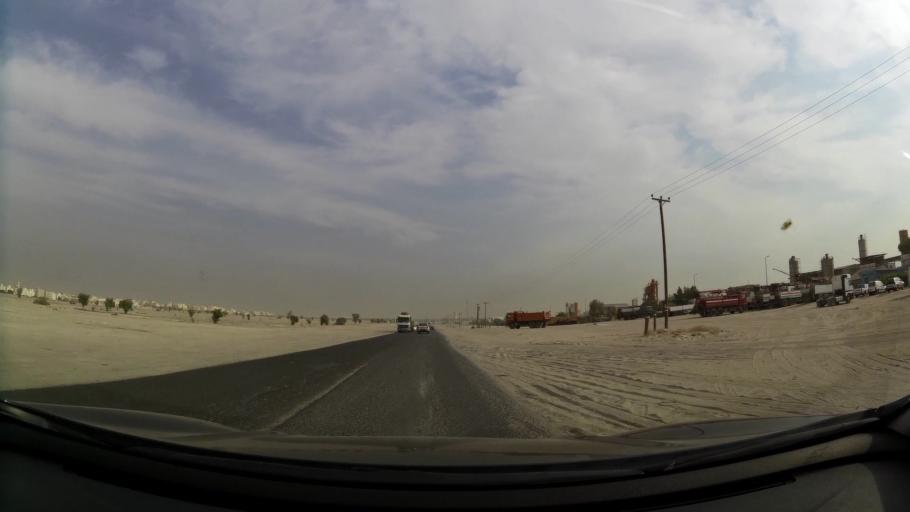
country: KW
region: Muhafazat al Jahra'
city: Al Jahra'
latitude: 29.3078
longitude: 47.7418
